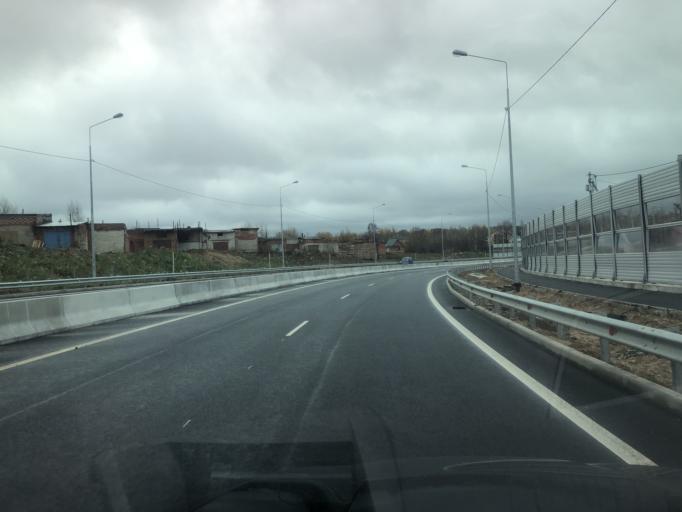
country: RU
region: Moskovskaya
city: Sergiyev Posad
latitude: 56.3380
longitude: 38.1212
